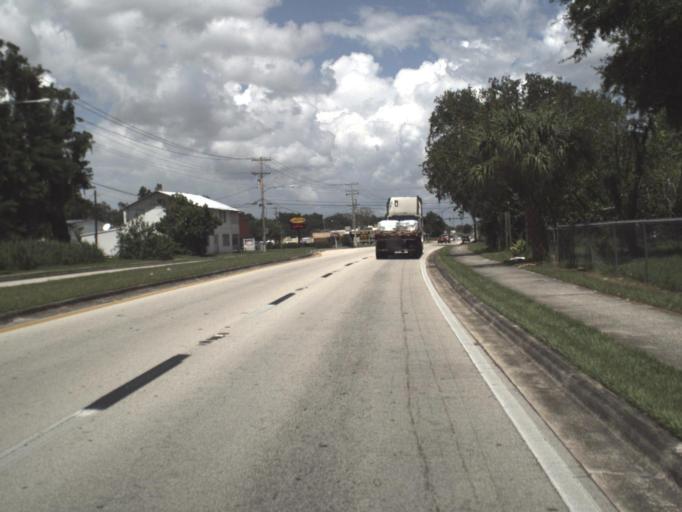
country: US
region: Florida
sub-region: Polk County
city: Bartow
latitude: 27.8940
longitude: -81.8285
